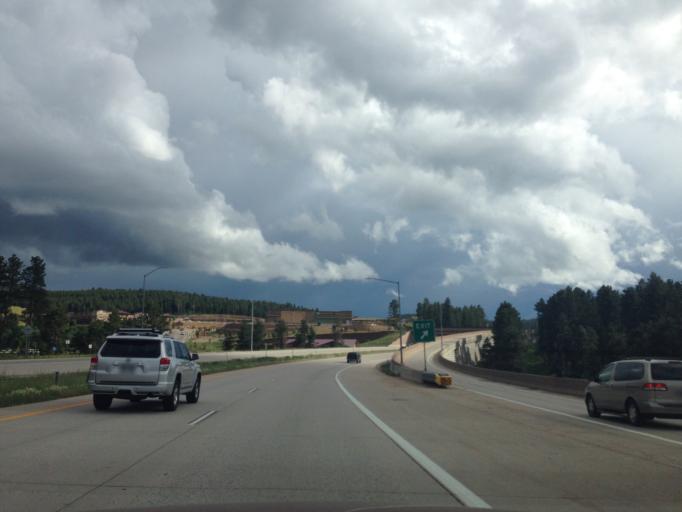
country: US
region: Colorado
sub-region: Jefferson County
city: Evergreen
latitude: 39.5329
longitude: -105.3045
